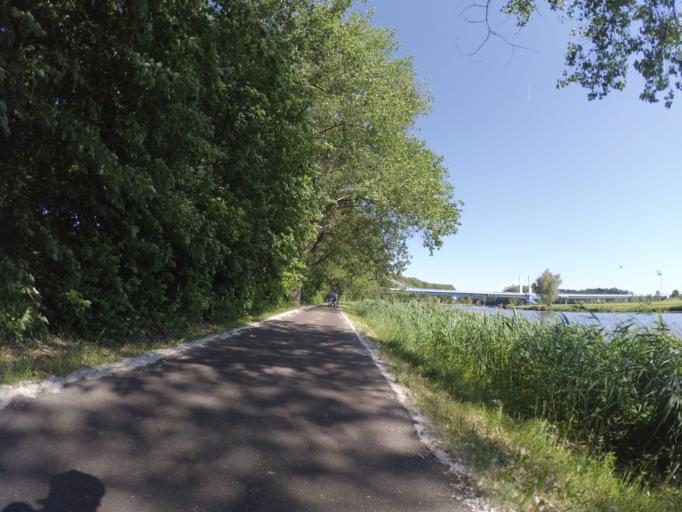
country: CZ
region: Central Bohemia
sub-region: Okres Nymburk
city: Podebrady
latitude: 50.1673
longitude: 15.0870
